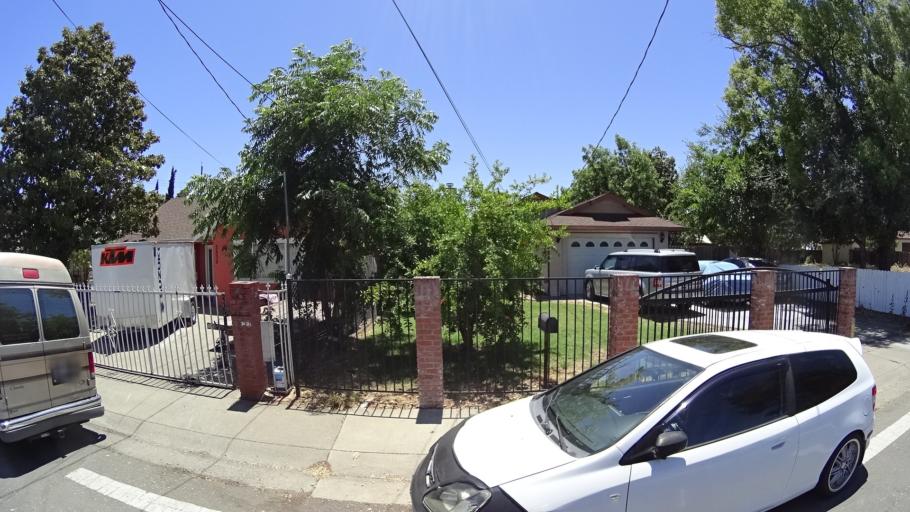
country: US
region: California
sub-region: Sacramento County
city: Parkway
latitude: 38.5376
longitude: -121.4685
